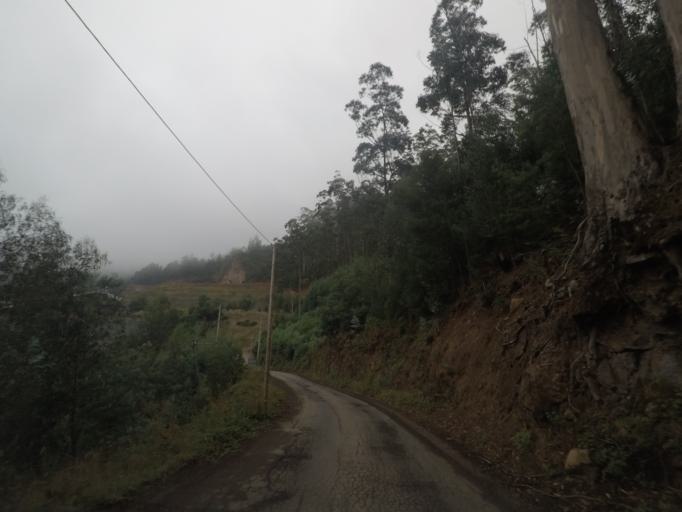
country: PT
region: Madeira
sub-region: Funchal
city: Nossa Senhora do Monte
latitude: 32.6914
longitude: -16.9077
